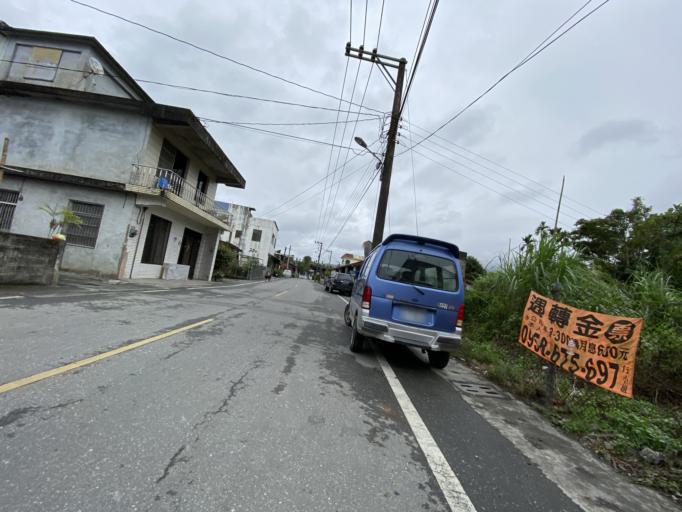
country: TW
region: Taiwan
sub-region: Hualien
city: Hualian
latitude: 23.6576
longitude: 121.4509
